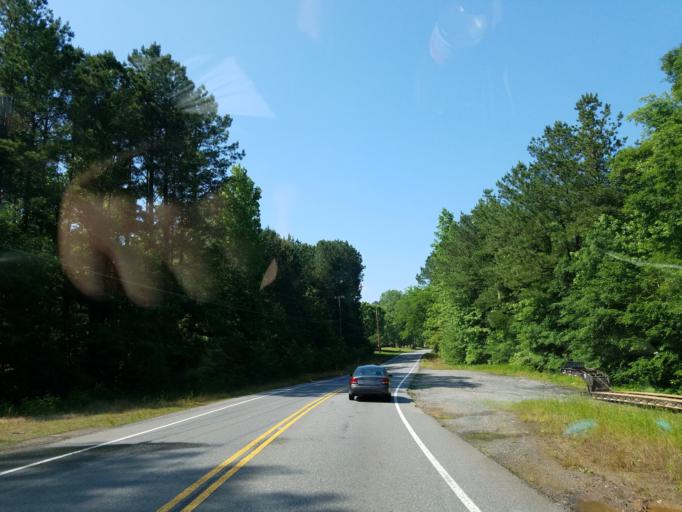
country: US
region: Georgia
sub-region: Cherokee County
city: Woodstock
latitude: 34.1243
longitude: -84.4930
